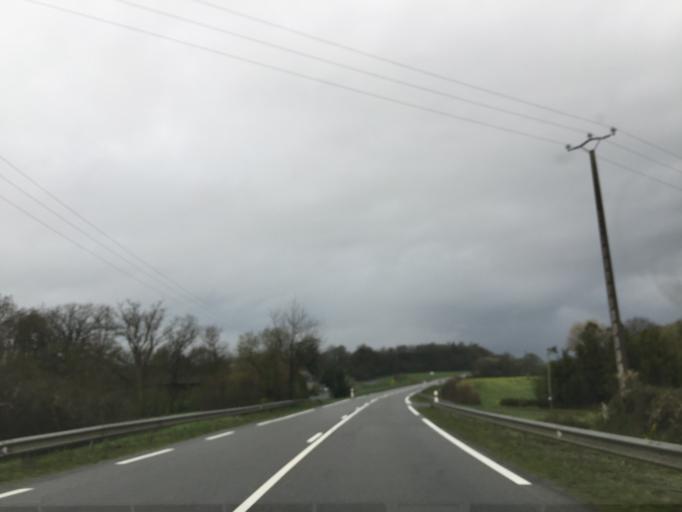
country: FR
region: Brittany
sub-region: Departement d'Ille-et-Vilaine
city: Martigne-Ferchaud
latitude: 47.8451
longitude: -1.3005
